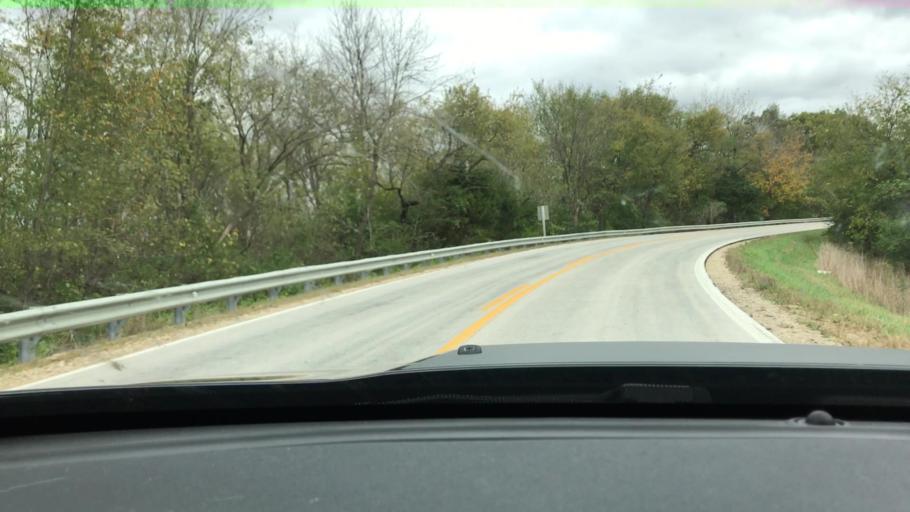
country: US
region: Illinois
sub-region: LaSalle County
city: Sheridan
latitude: 41.5309
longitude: -88.6921
